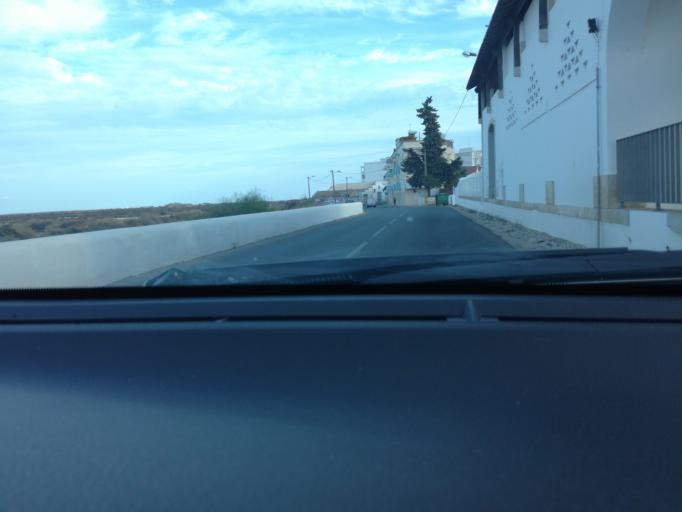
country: PT
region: Faro
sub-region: Olhao
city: Laranjeiro
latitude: 37.0603
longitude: -7.7516
